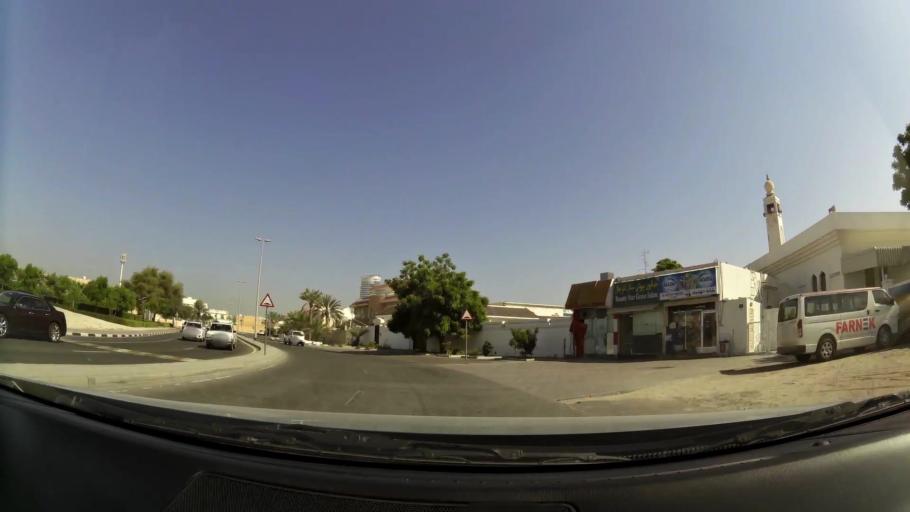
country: AE
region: Ash Shariqah
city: Sharjah
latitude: 25.2464
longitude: 55.2938
